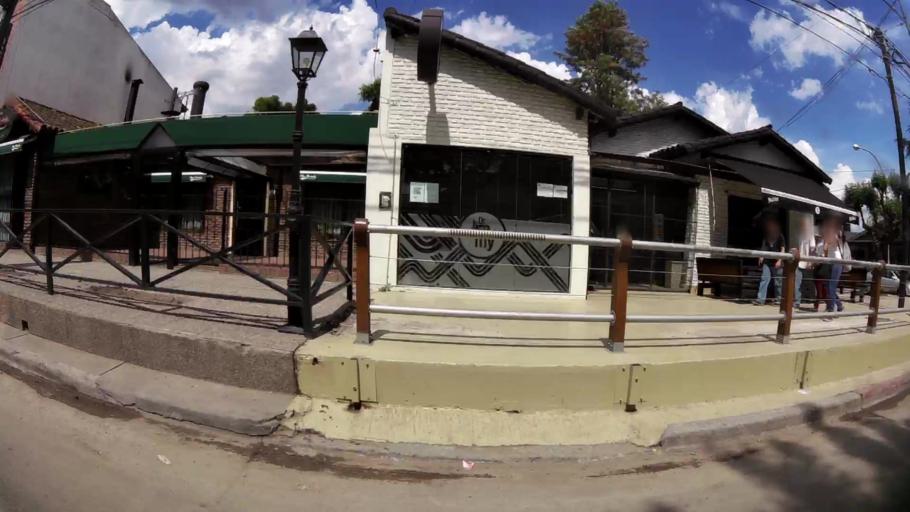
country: AR
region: Buenos Aires
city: Ituzaingo
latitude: -34.6447
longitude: -58.6570
